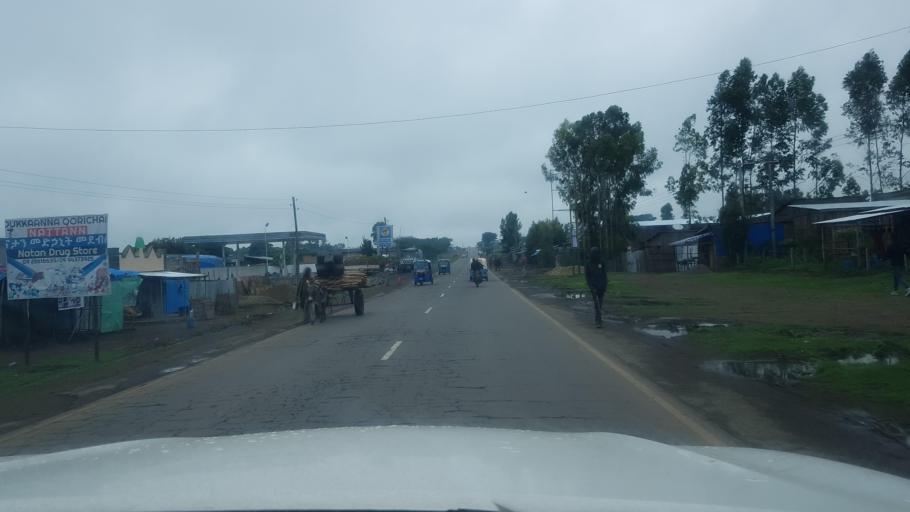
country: ET
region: Oromiya
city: Shashemene
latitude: 7.3732
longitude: 38.6717
